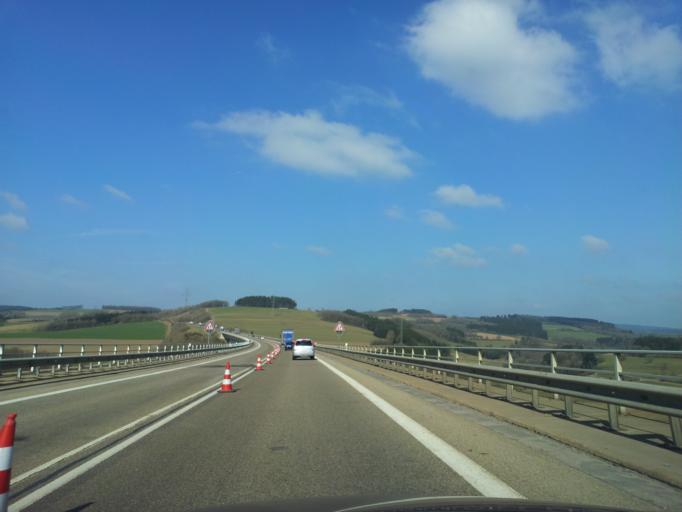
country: DE
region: Rheinland-Pfalz
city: Watzerath
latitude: 50.1885
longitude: 6.3848
